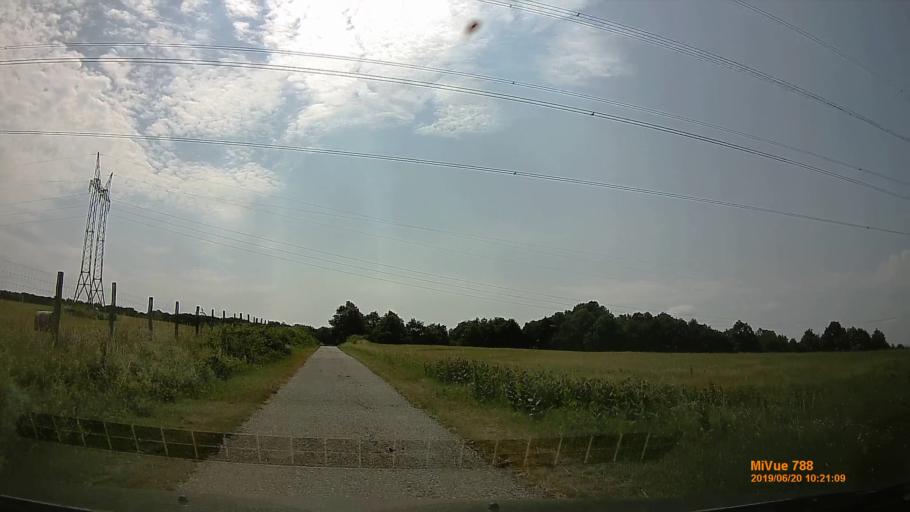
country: HU
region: Baranya
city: Mecseknadasd
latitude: 46.2102
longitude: 18.4743
